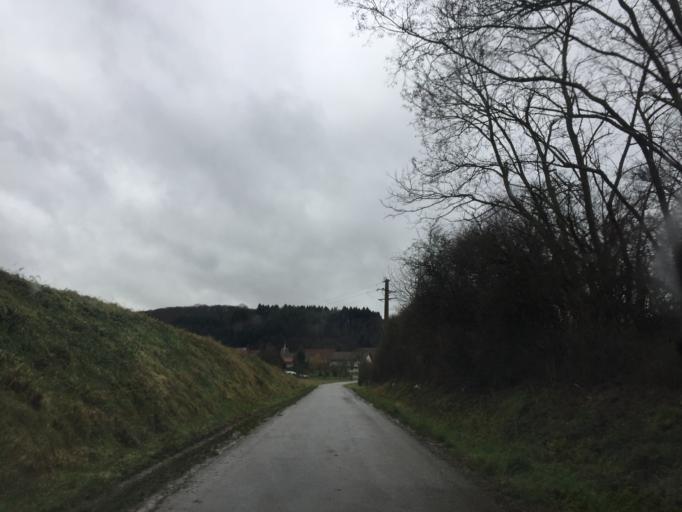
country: FR
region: Franche-Comte
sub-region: Departement du Jura
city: Orchamps
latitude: 47.2038
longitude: 5.6229
